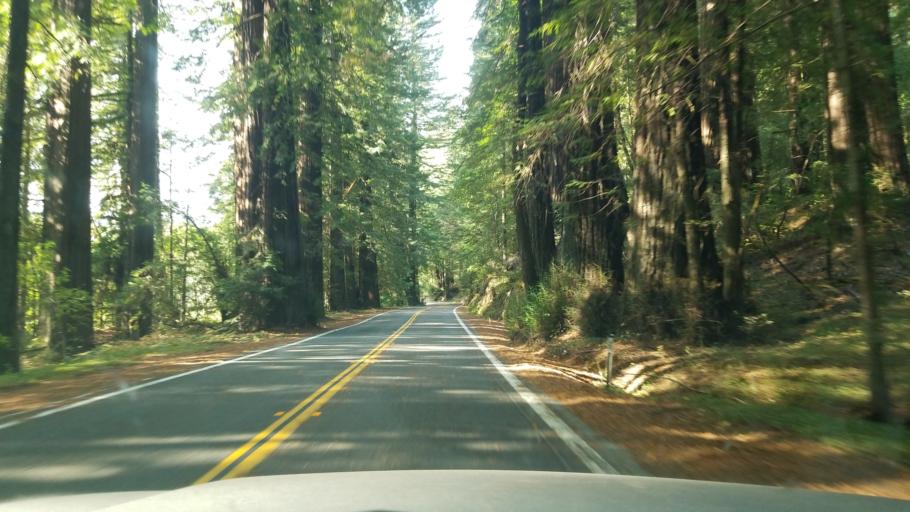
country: US
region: California
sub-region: Humboldt County
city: Redway
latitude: 40.2640
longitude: -123.8454
